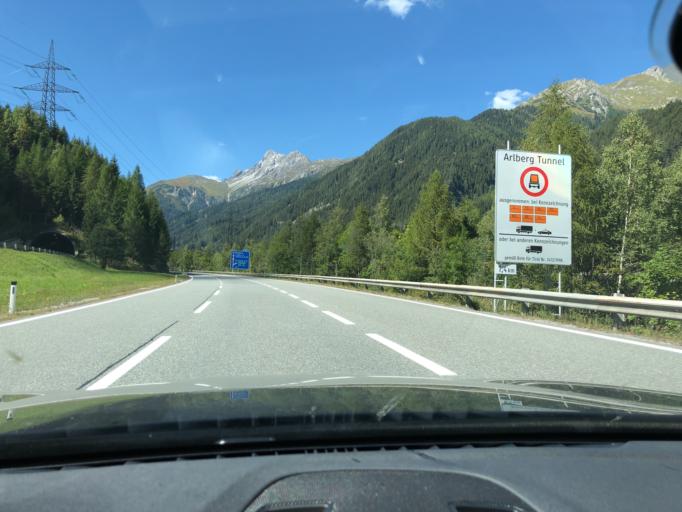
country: AT
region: Tyrol
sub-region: Politischer Bezirk Landeck
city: Flirsch
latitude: 47.1435
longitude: 10.3336
